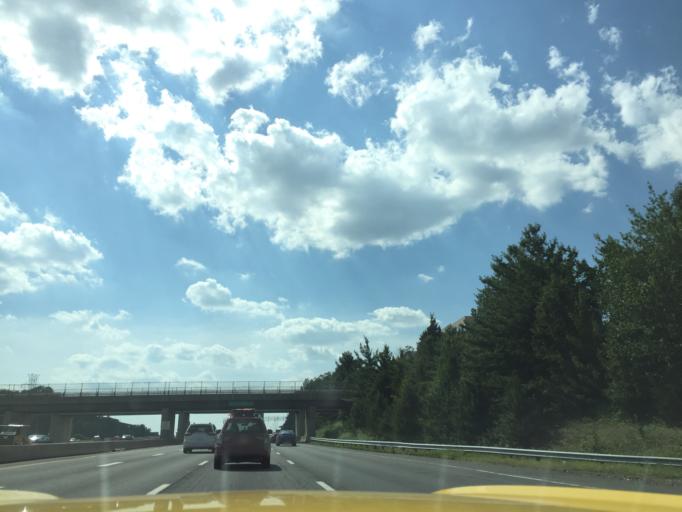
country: US
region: Virginia
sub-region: Fairfax County
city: Herndon
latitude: 38.9534
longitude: -77.3872
